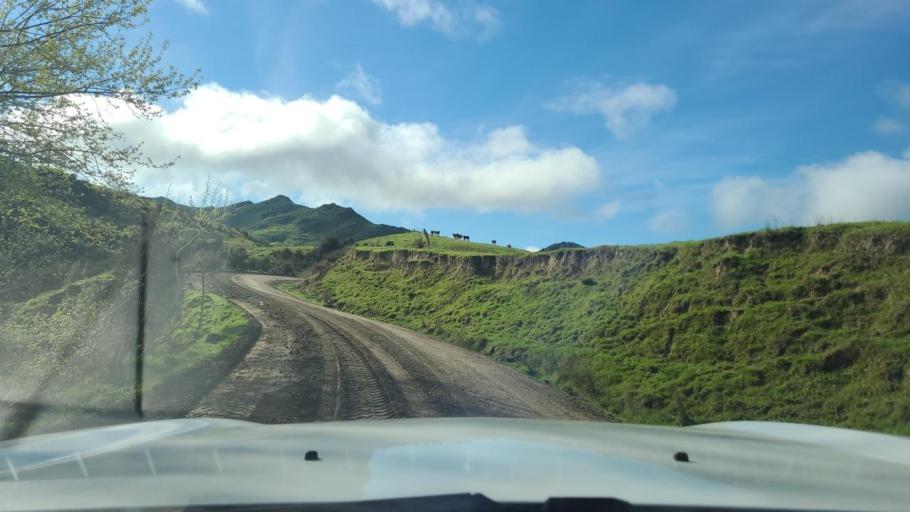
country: NZ
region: Wellington
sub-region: South Wairarapa District
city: Waipawa
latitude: -41.2451
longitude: 175.6944
